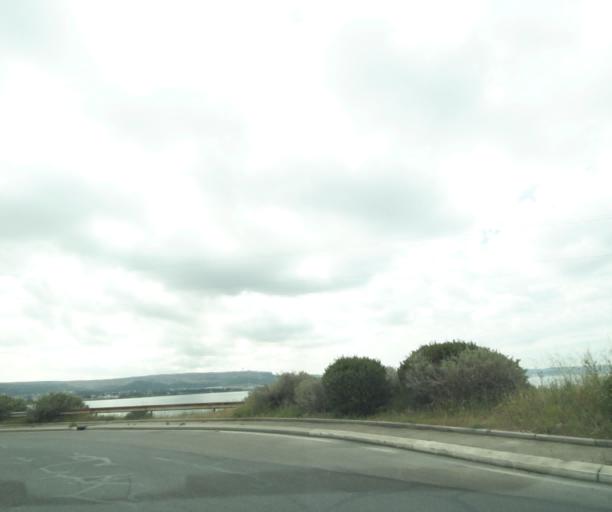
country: FR
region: Provence-Alpes-Cote d'Azur
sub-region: Departement des Bouches-du-Rhone
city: Berre-l'Etang
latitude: 43.4898
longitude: 5.1987
